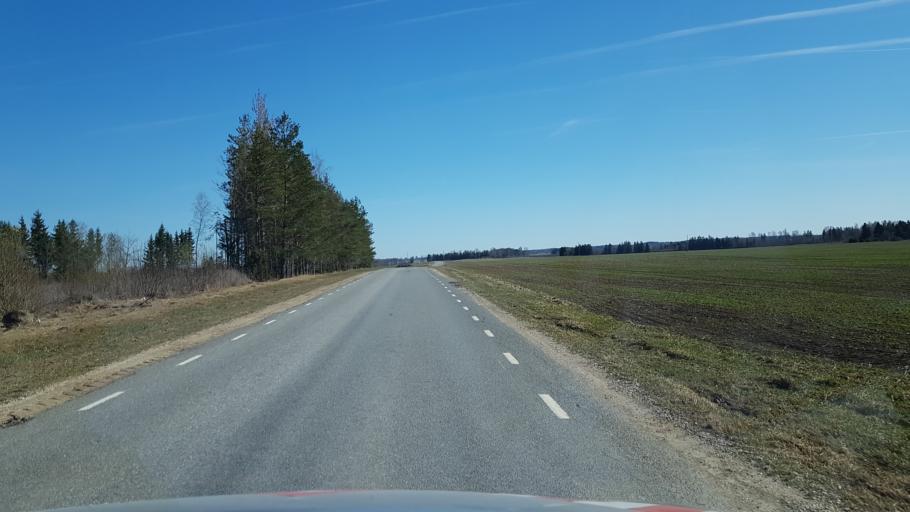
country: EE
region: Laeaene-Virumaa
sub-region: Someru vald
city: Someru
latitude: 59.3600
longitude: 26.4710
